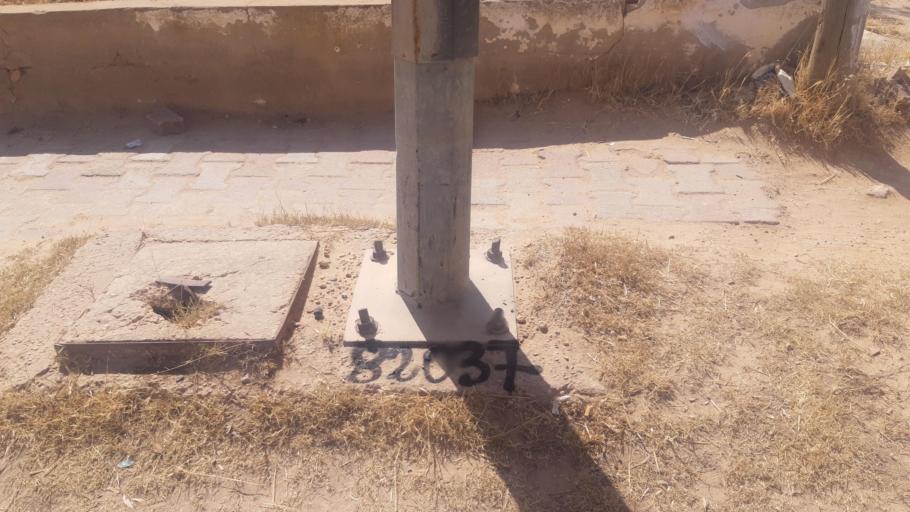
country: TN
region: Safaqis
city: Jabinyanah
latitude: 34.9776
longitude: 10.8921
